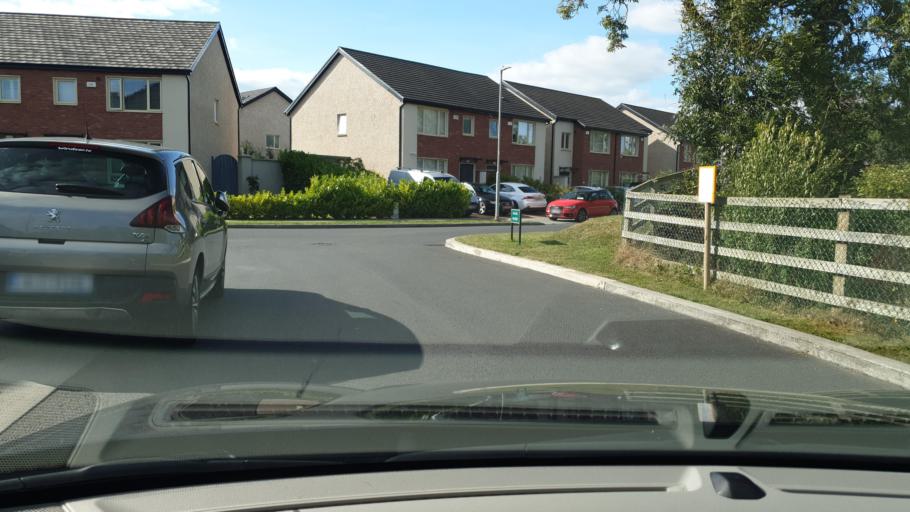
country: IE
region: Leinster
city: Hartstown
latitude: 53.3881
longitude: -6.4349
